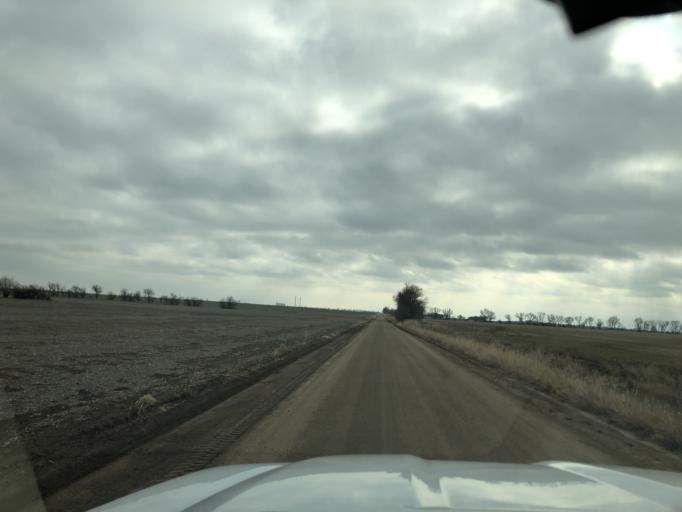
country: US
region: Kansas
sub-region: Reno County
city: Nickerson
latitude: 38.0174
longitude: -98.2158
